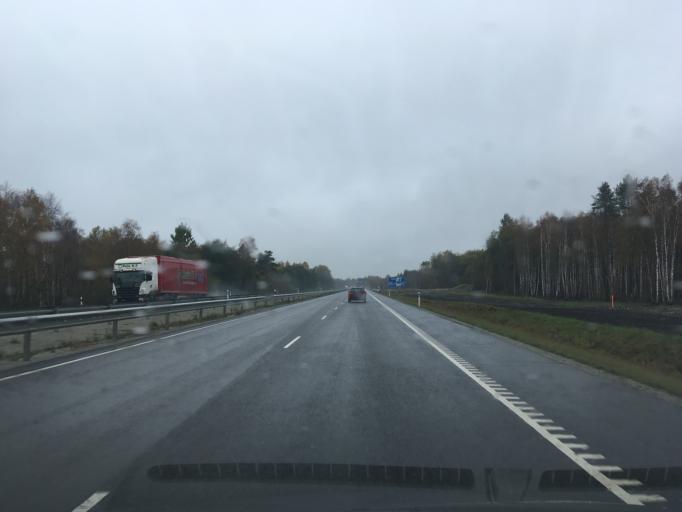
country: EE
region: Harju
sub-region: Saue vald
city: Laagri
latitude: 59.3127
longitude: 24.5980
